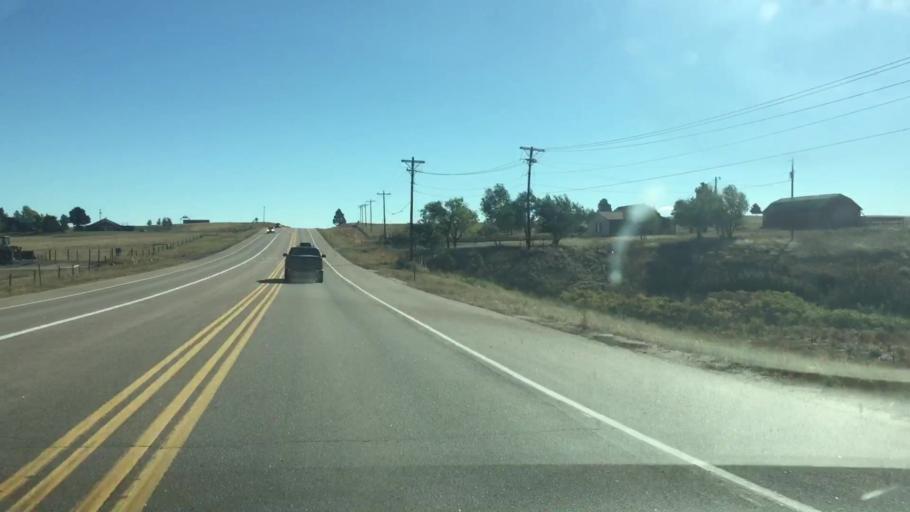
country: US
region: Colorado
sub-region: Elbert County
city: Elizabeth
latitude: 39.3613
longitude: -104.5515
